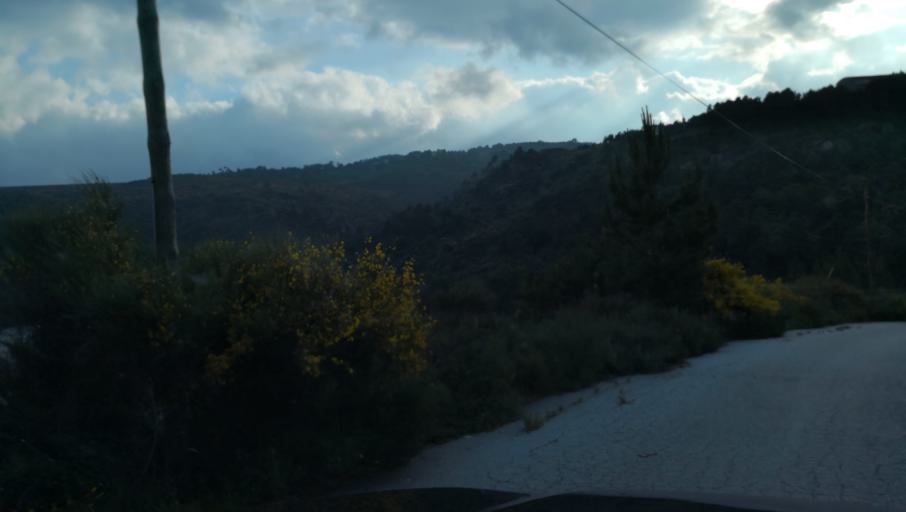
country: PT
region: Vila Real
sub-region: Vila Real
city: Vila Real
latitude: 41.2721
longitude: -7.7887
